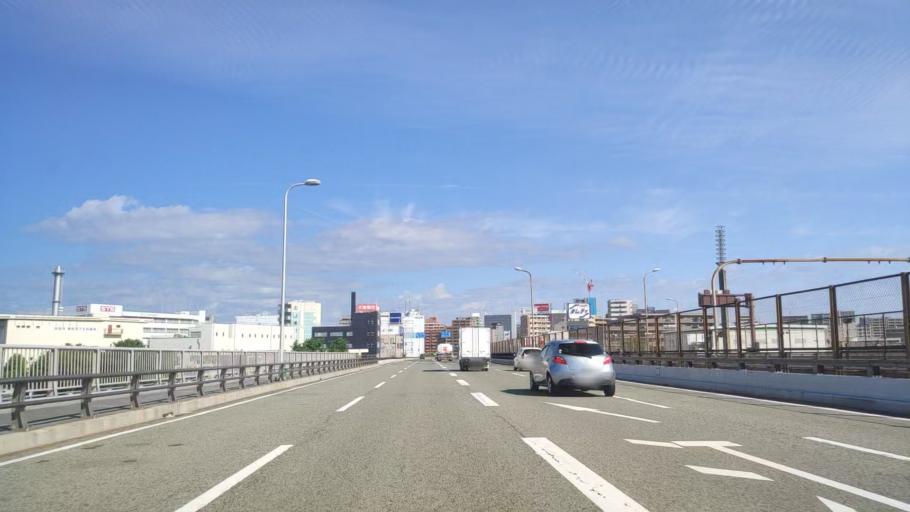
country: JP
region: Osaka
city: Suita
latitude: 34.7490
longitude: 135.4970
